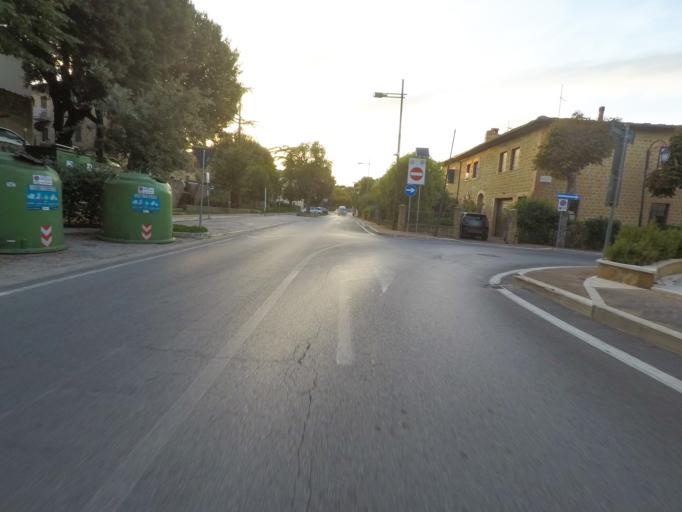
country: IT
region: Tuscany
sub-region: Provincia di Siena
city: Pienza
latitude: 43.0775
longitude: 11.6790
